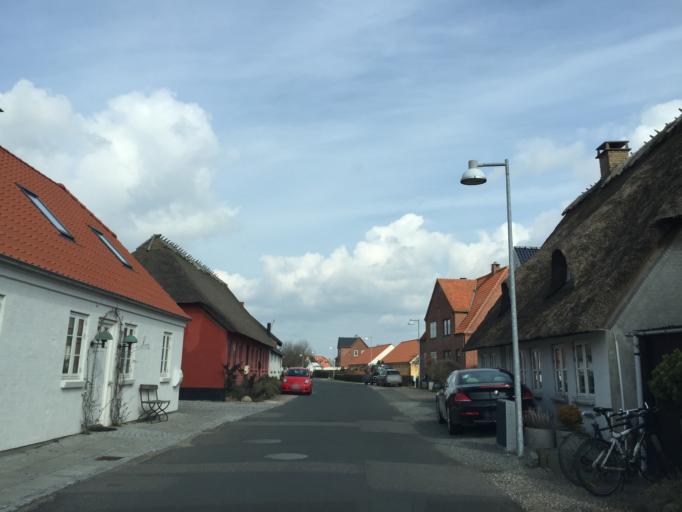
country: DK
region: South Denmark
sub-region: Odense Kommune
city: Stige
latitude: 55.4258
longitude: 10.4138
